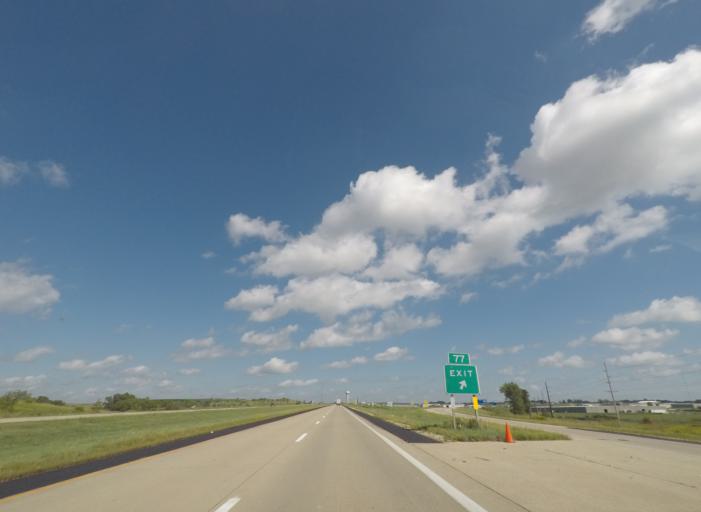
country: US
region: Iowa
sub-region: Dubuque County
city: Cascade
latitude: 42.3107
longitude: -91.0026
